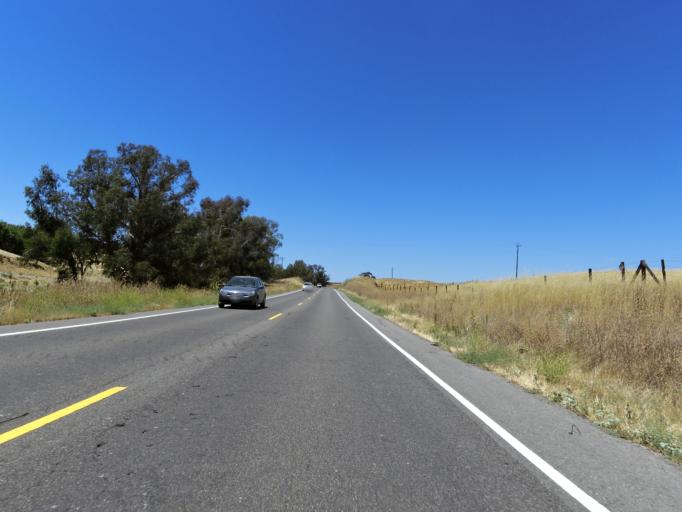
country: US
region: California
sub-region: Madera County
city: Bonadelle Ranchos-Madera Ranchos
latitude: 36.9988
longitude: -119.7288
